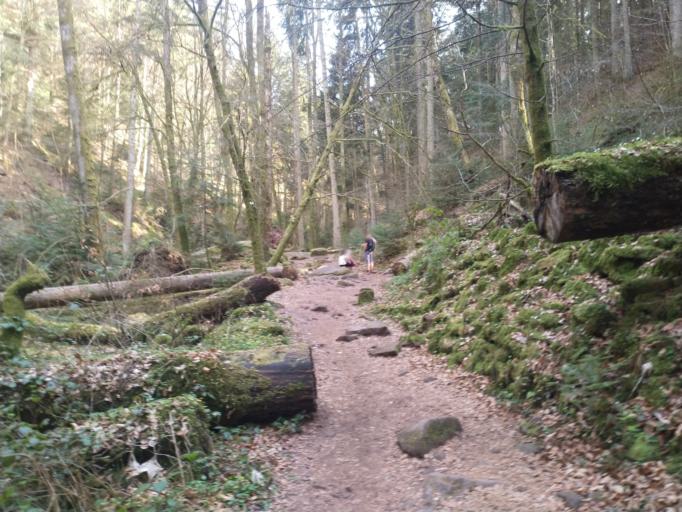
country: DE
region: Baden-Wuerttemberg
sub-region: Karlsruhe Region
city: Bad Liebenzell
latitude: 48.7987
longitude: 8.7442
